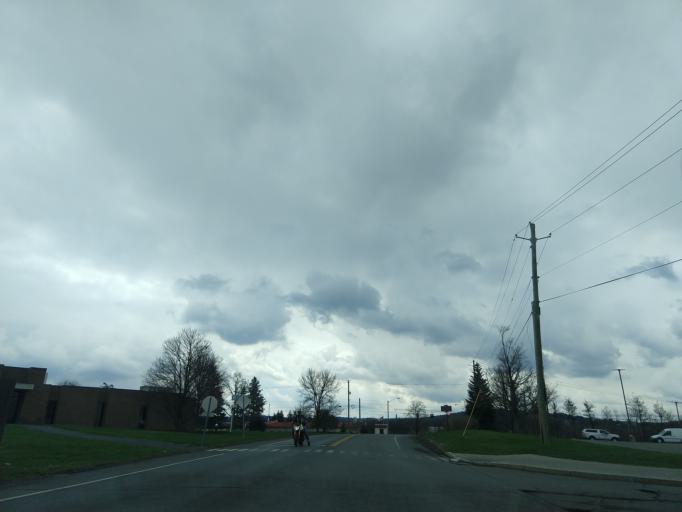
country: US
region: New York
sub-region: Tompkins County
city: East Ithaca
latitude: 42.4477
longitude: -76.4617
